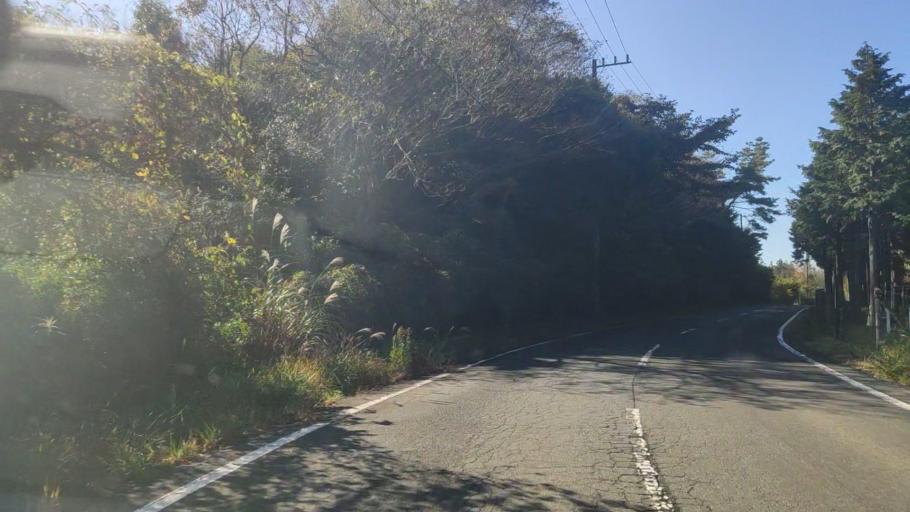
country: JP
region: Shizuoka
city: Atami
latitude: 35.0463
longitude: 139.0281
